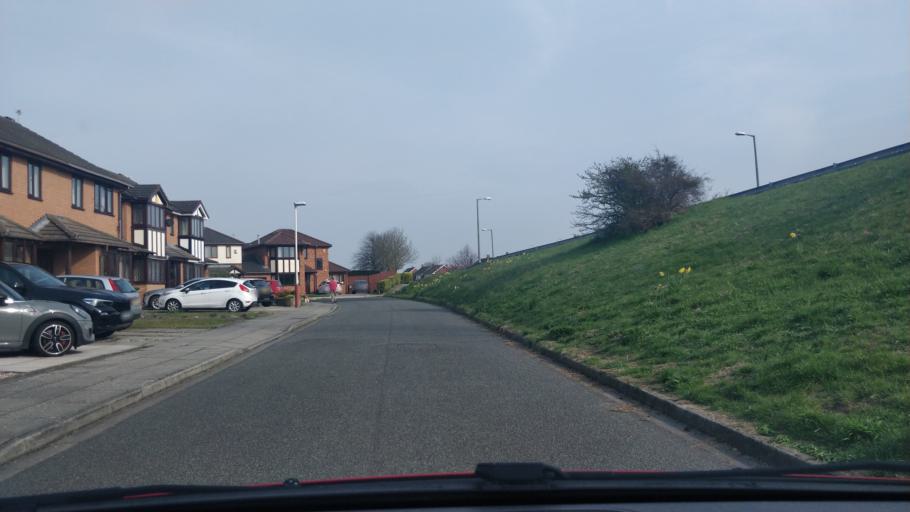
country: GB
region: England
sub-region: Sefton
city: Formby
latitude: 53.5987
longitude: -3.0440
